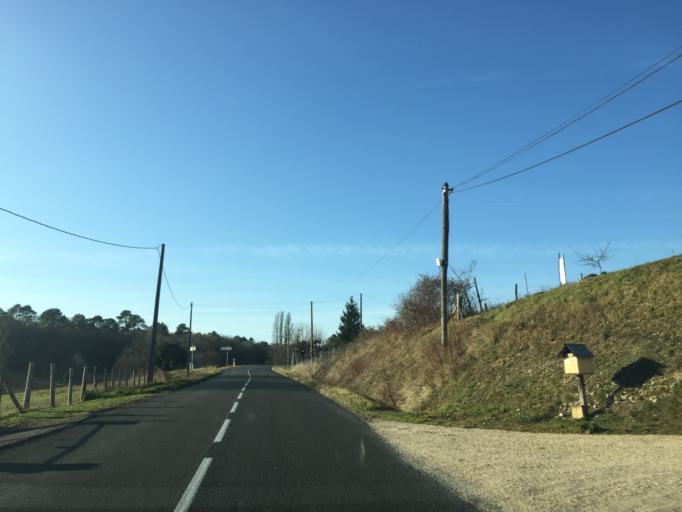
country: FR
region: Aquitaine
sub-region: Departement de la Dordogne
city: Neuvic
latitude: 45.1417
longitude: 0.4447
